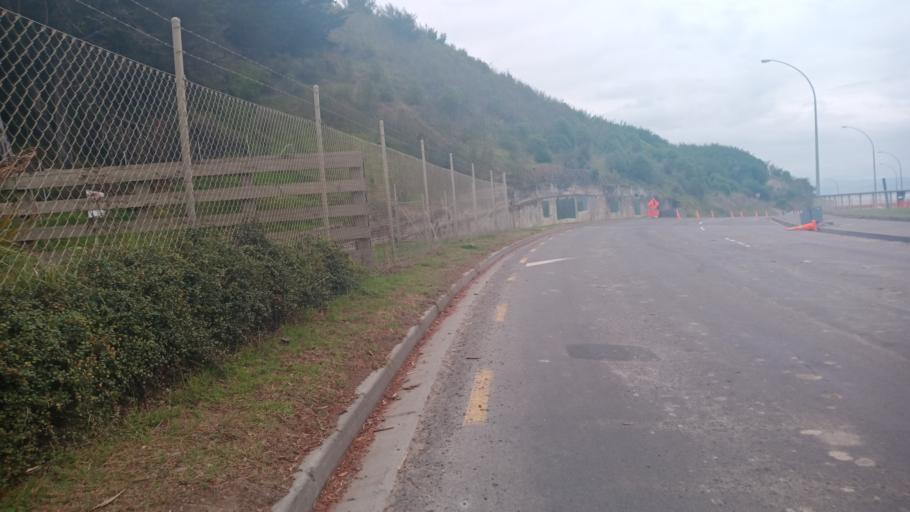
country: NZ
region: Gisborne
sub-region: Gisborne District
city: Gisborne
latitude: -38.6728
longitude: 178.0304
